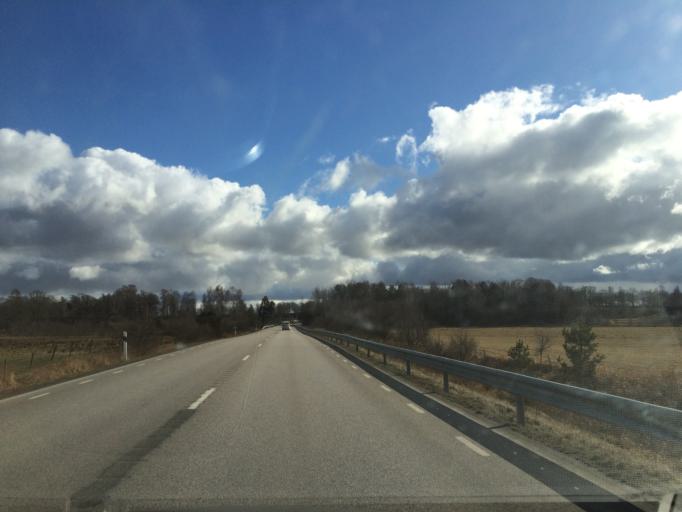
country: SE
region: Vaestra Goetaland
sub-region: Skara Kommun
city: Skara
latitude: 58.2897
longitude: 13.4785
